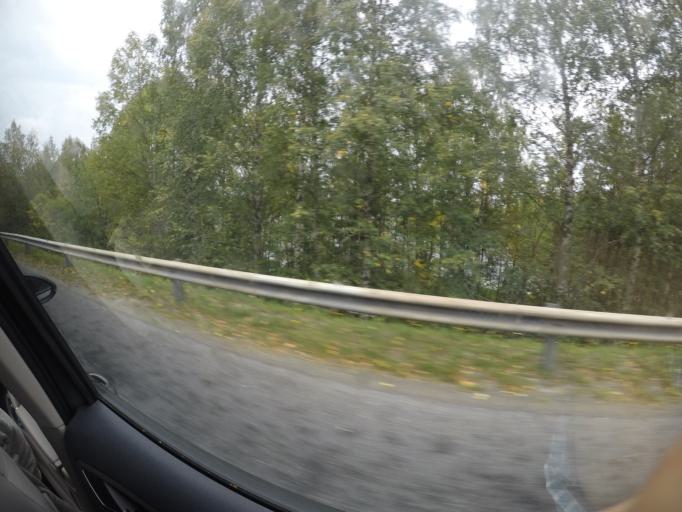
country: FI
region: Haeme
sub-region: Haemeenlinna
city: Parola
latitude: 61.0647
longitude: 24.3925
